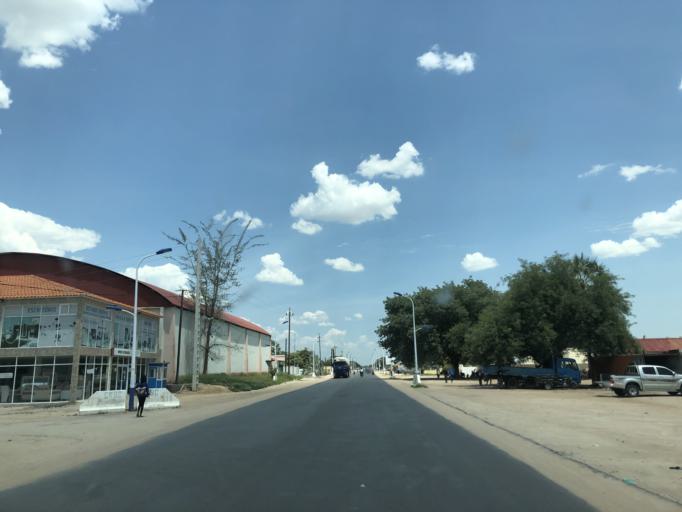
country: AO
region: Cunene
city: Ondjiva
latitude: -17.0823
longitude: 15.7390
